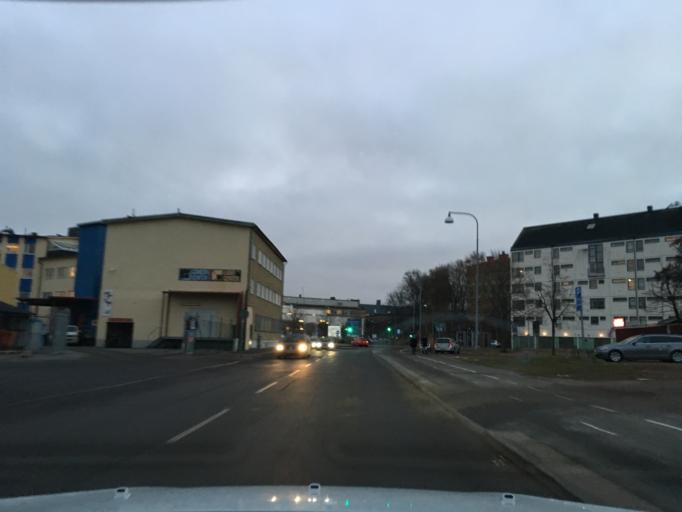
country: SE
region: Vaestra Goetaland
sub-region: Goteborg
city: Majorna
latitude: 57.7085
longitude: 11.9331
